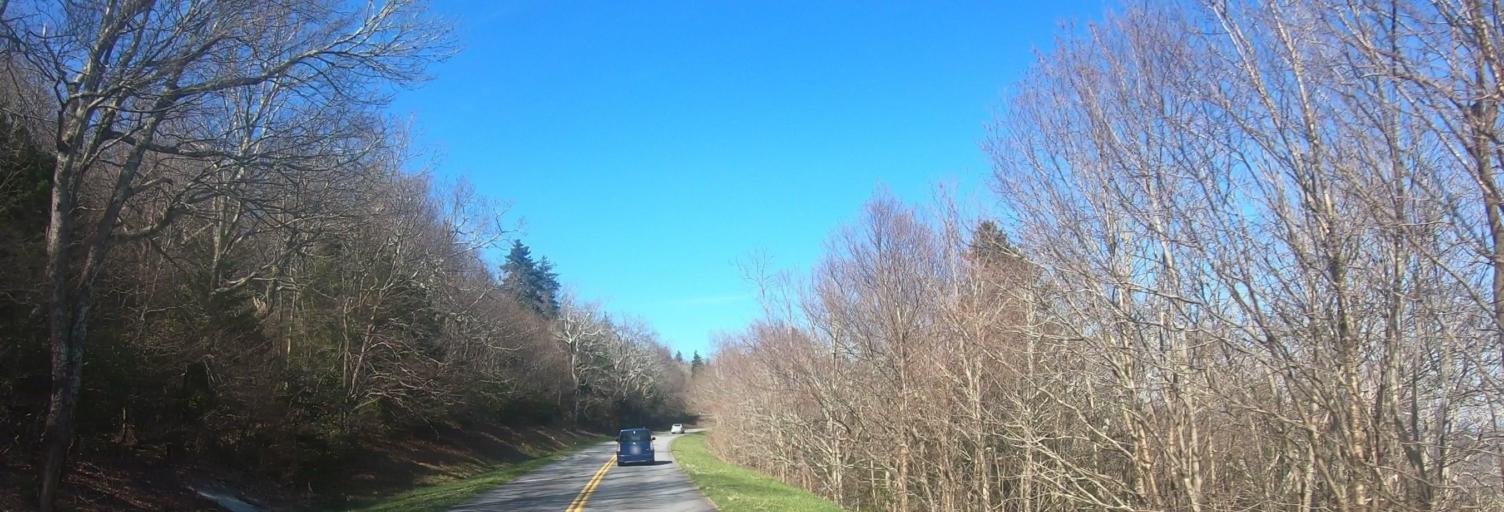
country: US
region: North Carolina
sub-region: Watauga County
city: Foscoe
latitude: 36.0978
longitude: -81.7829
